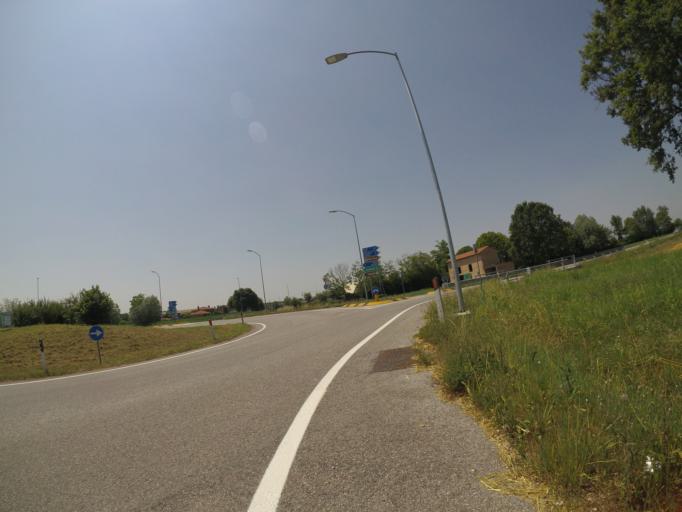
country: IT
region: Friuli Venezia Giulia
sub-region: Provincia di Udine
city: Varmo
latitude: 45.8950
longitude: 13.0104
